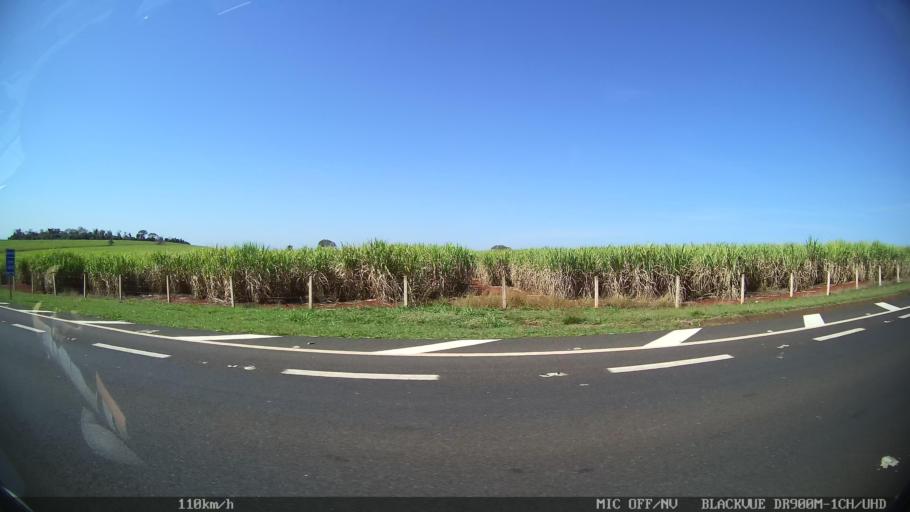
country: BR
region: Sao Paulo
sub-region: Batatais
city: Batatais
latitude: -20.7902
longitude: -47.5591
